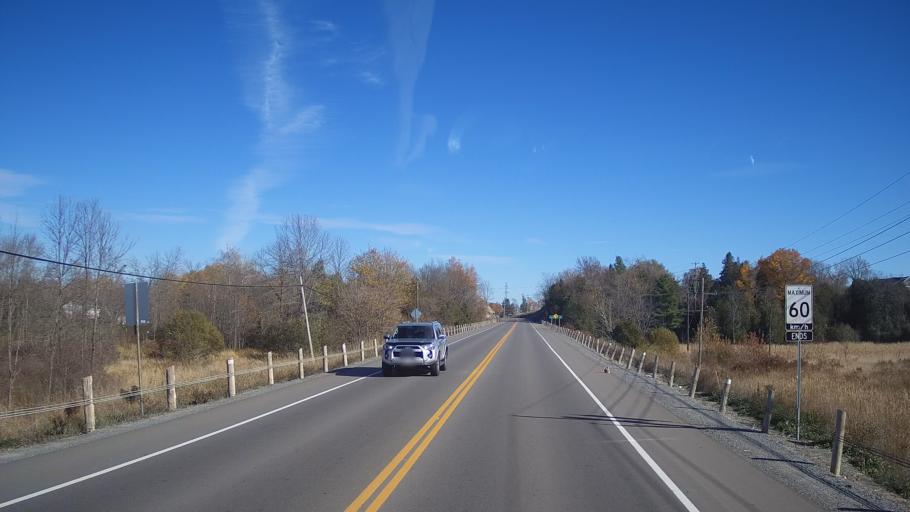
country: CA
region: Ontario
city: Kingston
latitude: 44.4055
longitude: -76.6536
